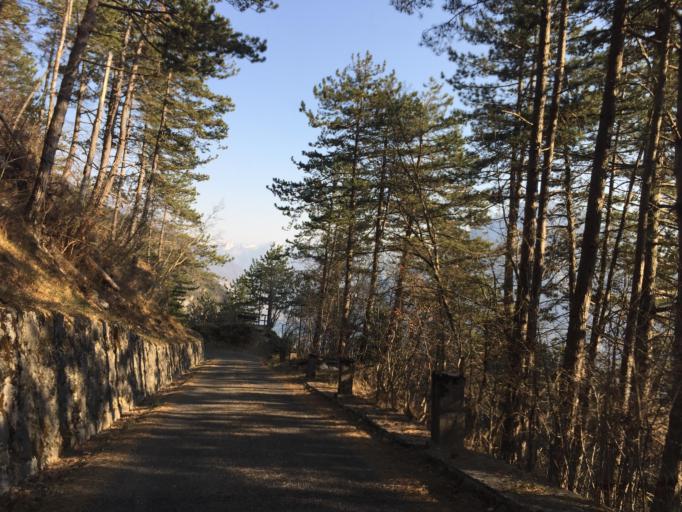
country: IT
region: Friuli Venezia Giulia
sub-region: Provincia di Udine
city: Amaro
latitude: 46.3870
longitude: 13.0829
